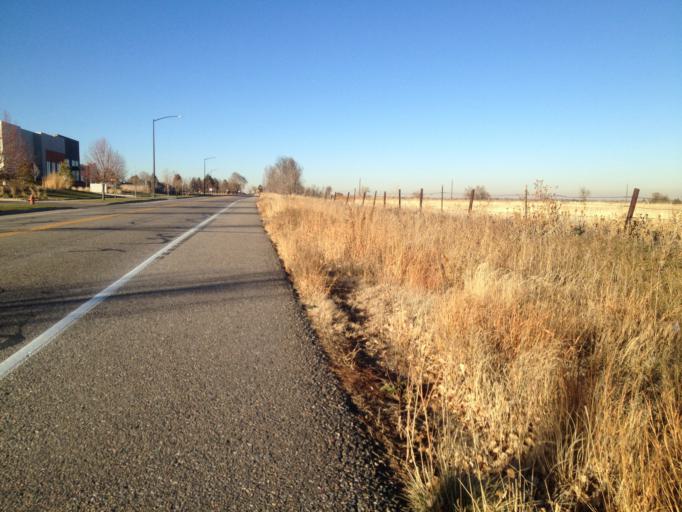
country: US
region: Colorado
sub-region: Boulder County
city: Louisville
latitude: 39.9686
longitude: -105.1093
